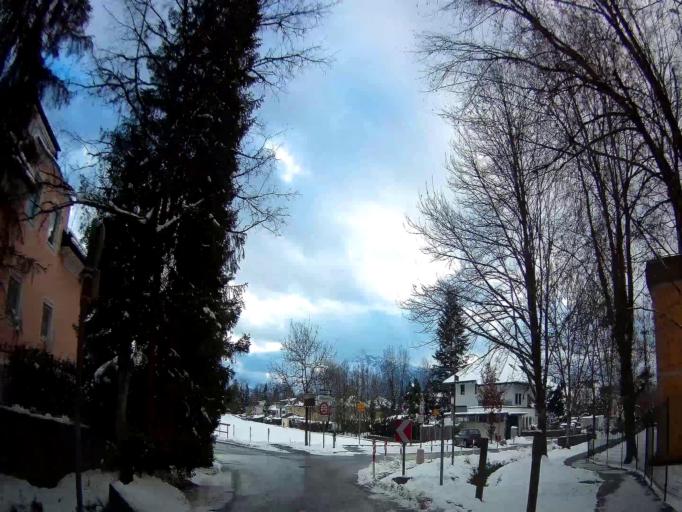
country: AT
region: Salzburg
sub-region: Salzburg Stadt
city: Salzburg
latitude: 47.7981
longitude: 13.0830
